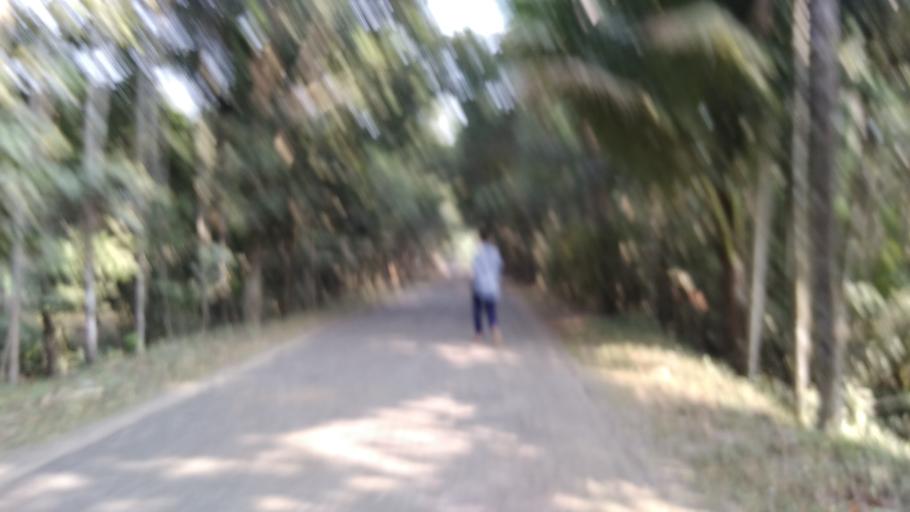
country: BD
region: Barisal
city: Mehendiganj
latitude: 22.9770
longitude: 90.4167
